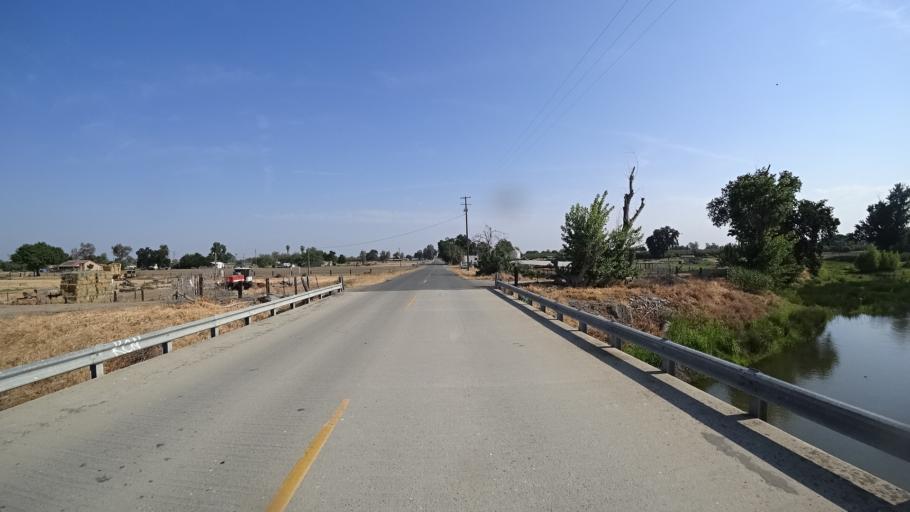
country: US
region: California
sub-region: Kings County
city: Lemoore
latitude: 36.3513
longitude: -119.8340
